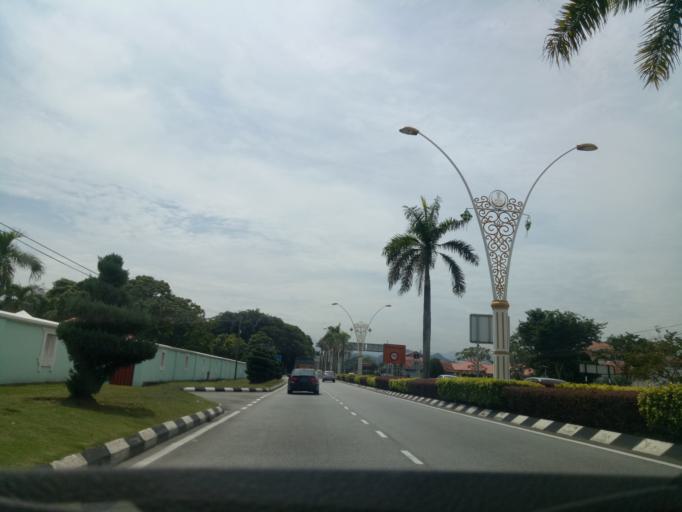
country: MY
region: Perak
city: Ipoh
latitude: 4.5930
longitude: 101.0913
